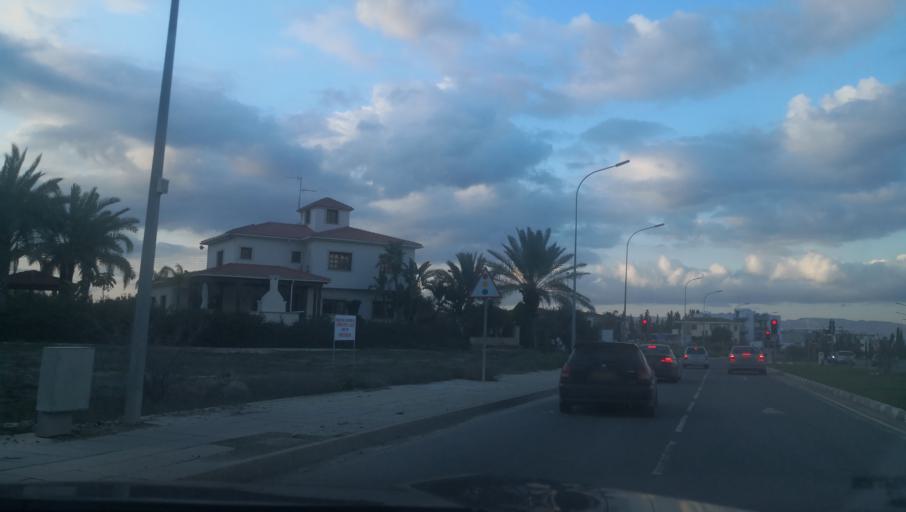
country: CY
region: Lefkosia
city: Tseri
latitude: 35.0987
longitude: 33.3139
